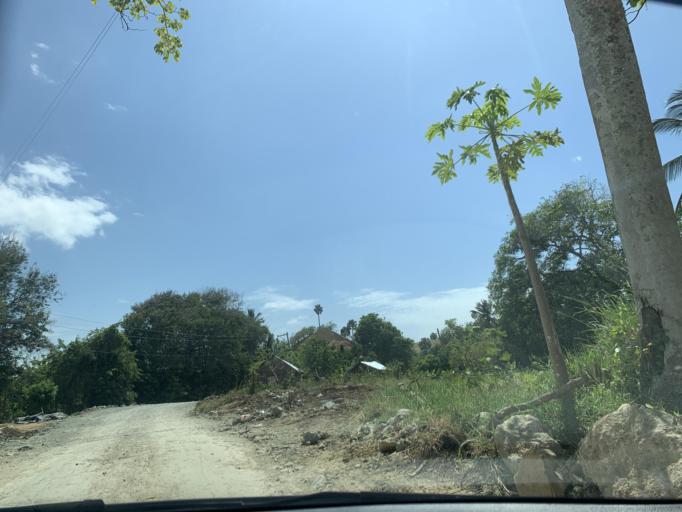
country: DO
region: Puerto Plata
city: Luperon
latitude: 19.8827
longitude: -70.8381
